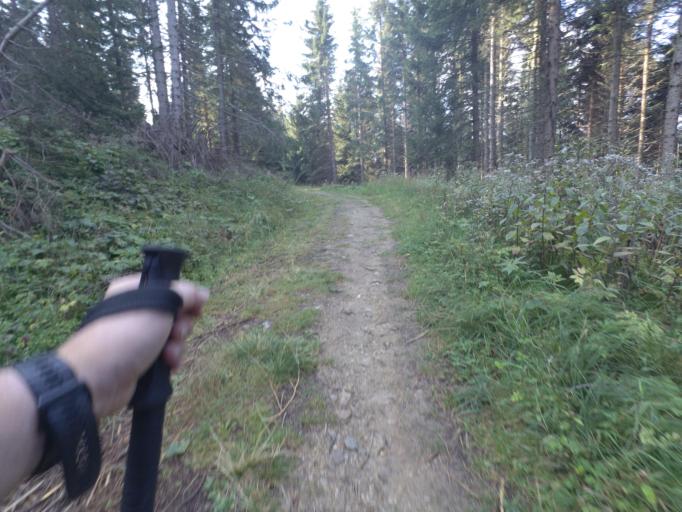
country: AT
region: Salzburg
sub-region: Politischer Bezirk Sankt Johann im Pongau
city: Kleinarl
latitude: 47.2702
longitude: 13.2631
